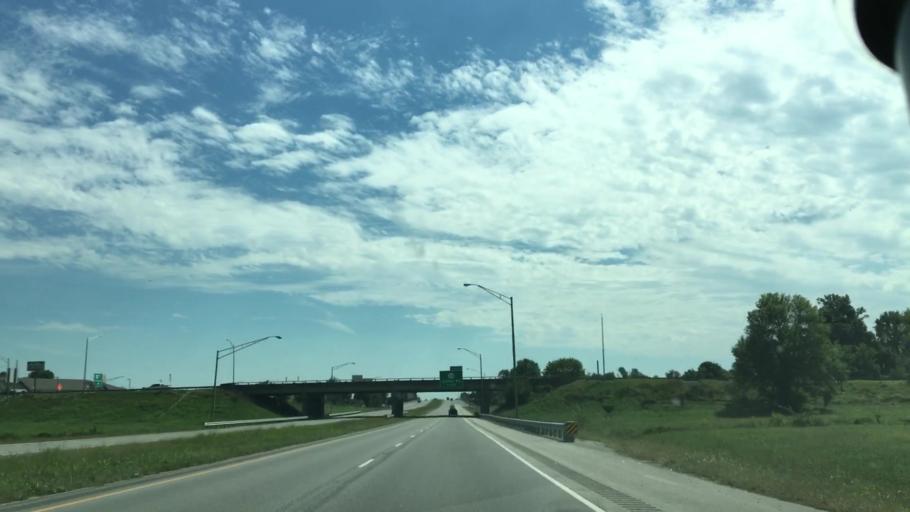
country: US
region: Kentucky
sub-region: Daviess County
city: Owensboro
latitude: 37.7567
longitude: -87.1596
